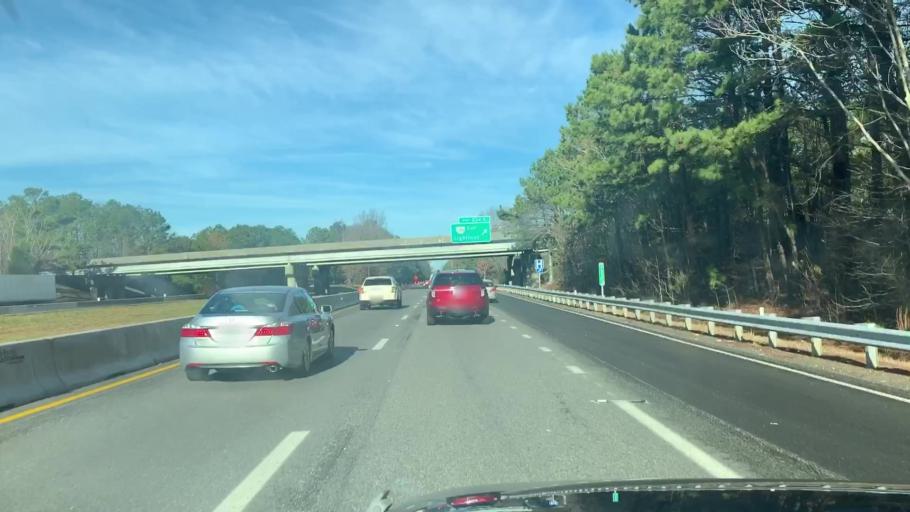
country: US
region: Virginia
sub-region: James City County
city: Williamsburg
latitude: 37.3519
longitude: -76.7301
